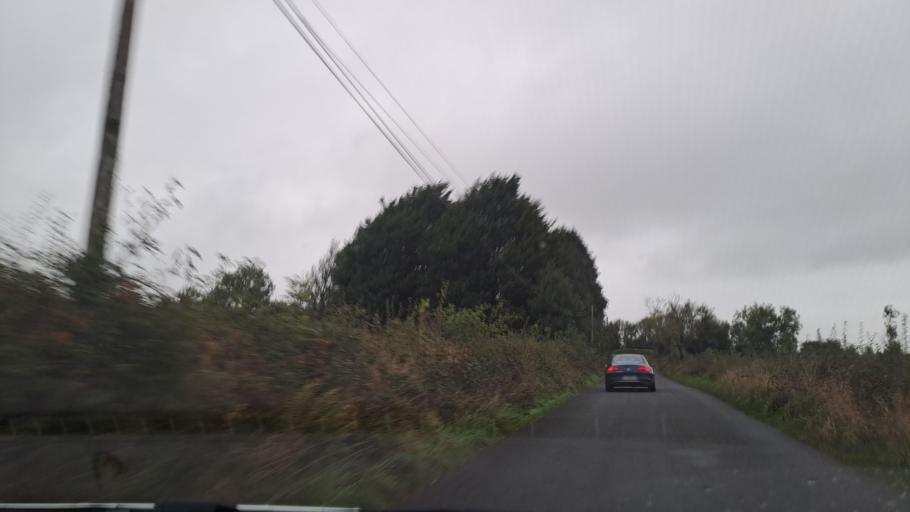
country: IE
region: Ulster
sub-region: County Monaghan
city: Monaghan
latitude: 54.2081
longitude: -6.9081
